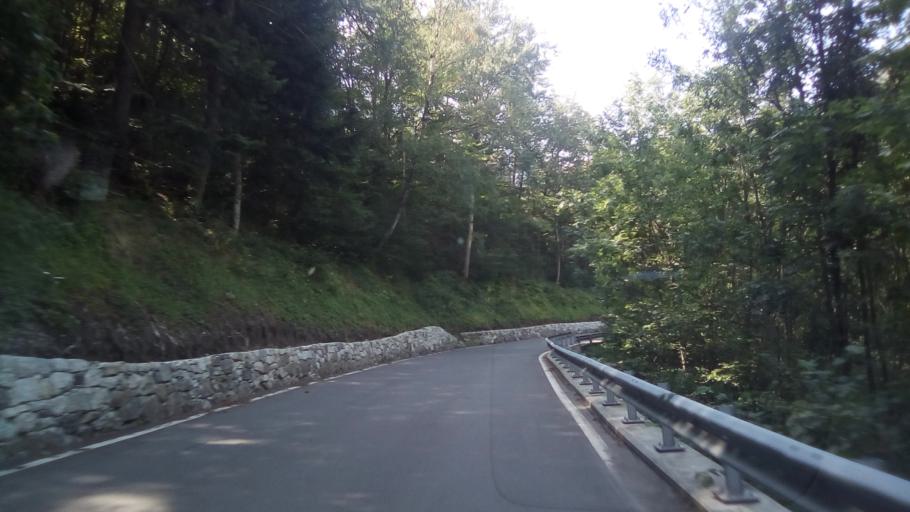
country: CH
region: Valais
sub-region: Martigny District
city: Martigny-Ville
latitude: 46.0782
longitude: 7.0813
